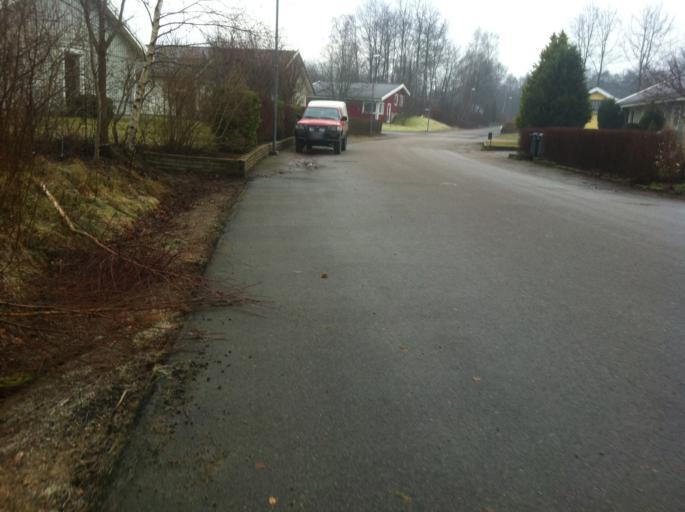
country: SE
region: Skane
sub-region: Perstorps Kommun
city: Perstorp
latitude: 56.1488
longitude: 13.3758
